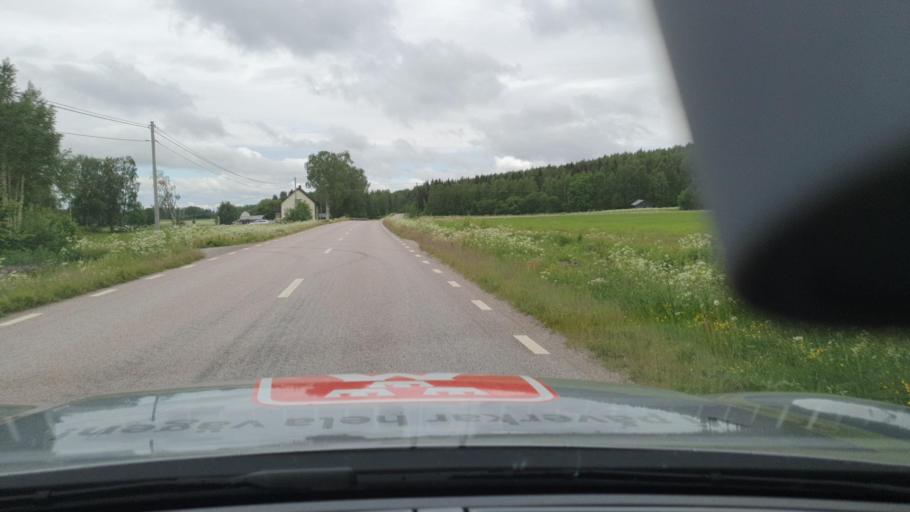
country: SE
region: Norrbotten
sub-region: Lulea Kommun
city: Ranea
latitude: 65.9034
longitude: 22.2122
